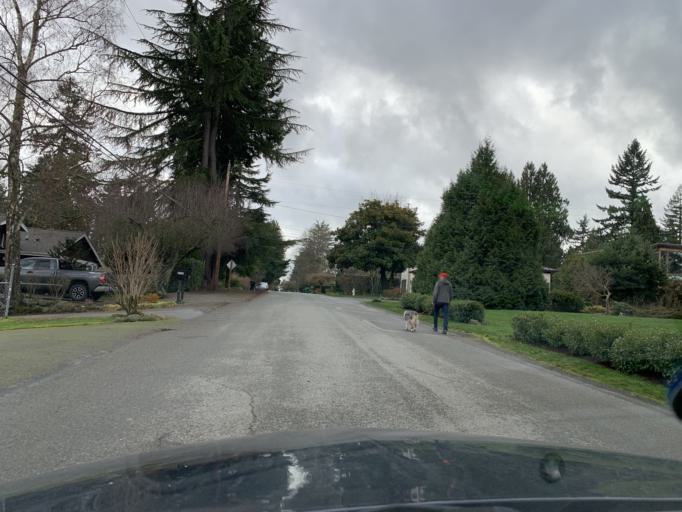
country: US
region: Washington
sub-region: King County
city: Mercer Island
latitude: 47.5839
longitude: -122.2404
